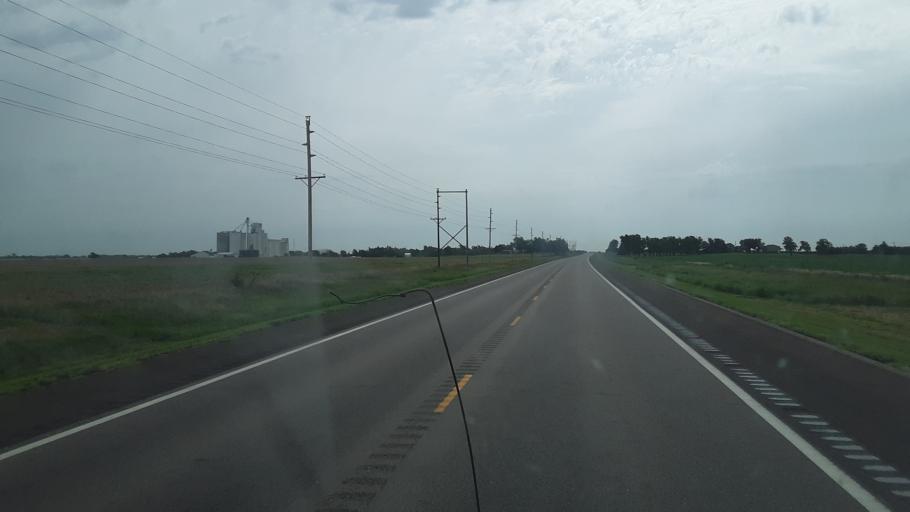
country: US
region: Kansas
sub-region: Stafford County
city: Stafford
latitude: 37.9550
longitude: -98.5056
